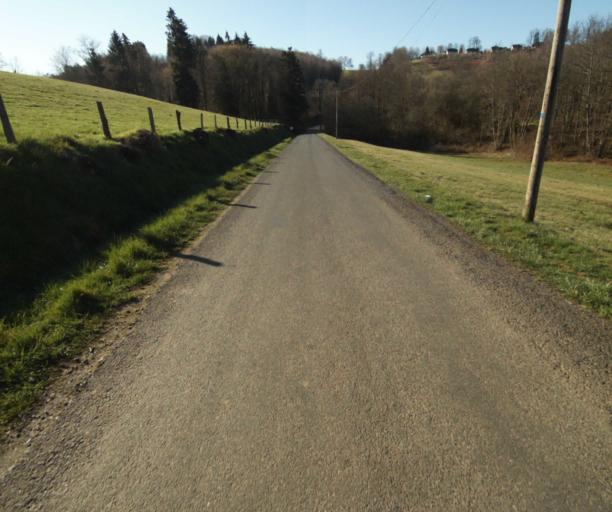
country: FR
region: Limousin
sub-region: Departement de la Correze
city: Seilhac
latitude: 45.3785
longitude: 1.7507
